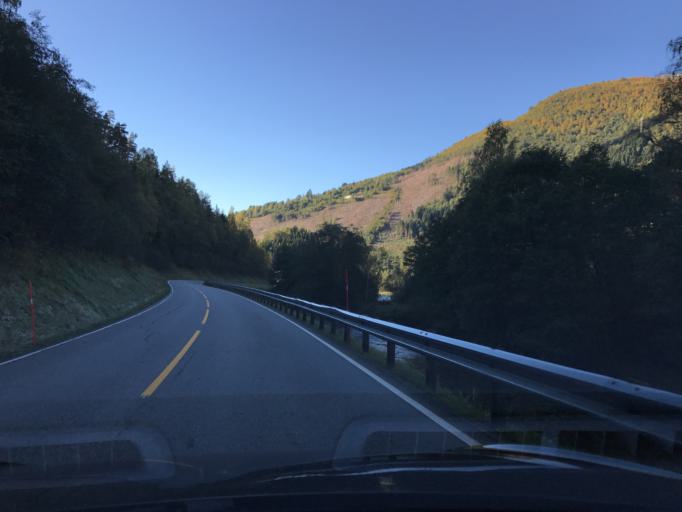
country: NO
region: More og Romsdal
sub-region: Norddal
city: Valldal
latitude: 62.3099
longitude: 7.2660
